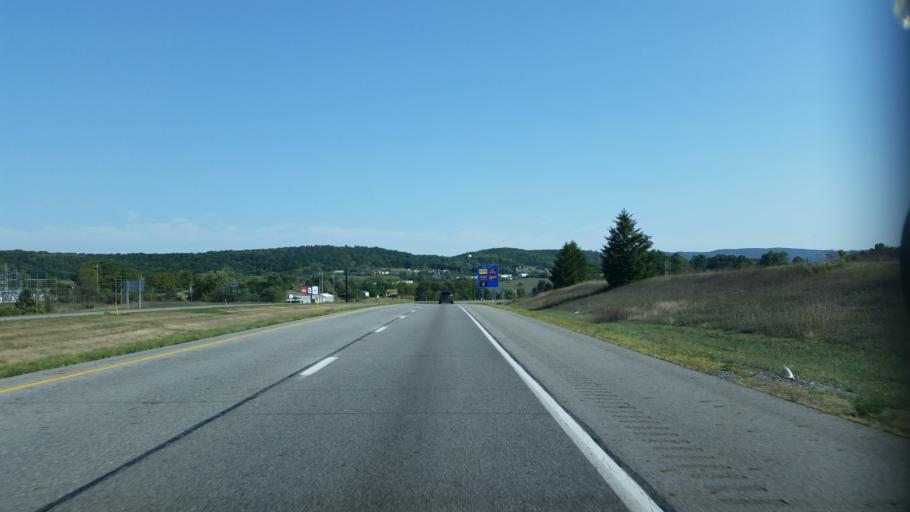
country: US
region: Pennsylvania
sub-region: Bedford County
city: Bedford
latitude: 40.0732
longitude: -78.5217
